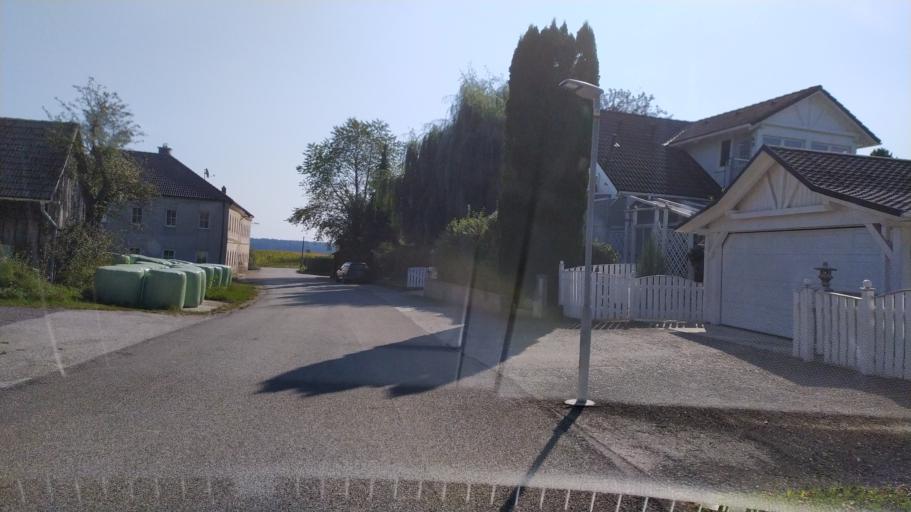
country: AT
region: Lower Austria
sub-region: Politischer Bezirk Amstetten
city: Zeillern
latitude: 48.1115
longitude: 14.7362
